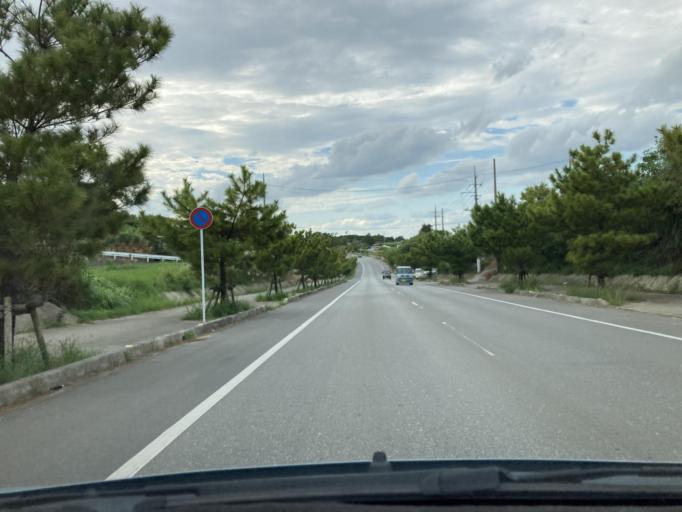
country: JP
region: Okinawa
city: Katsuren-haebaru
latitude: 26.3294
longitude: 127.8906
